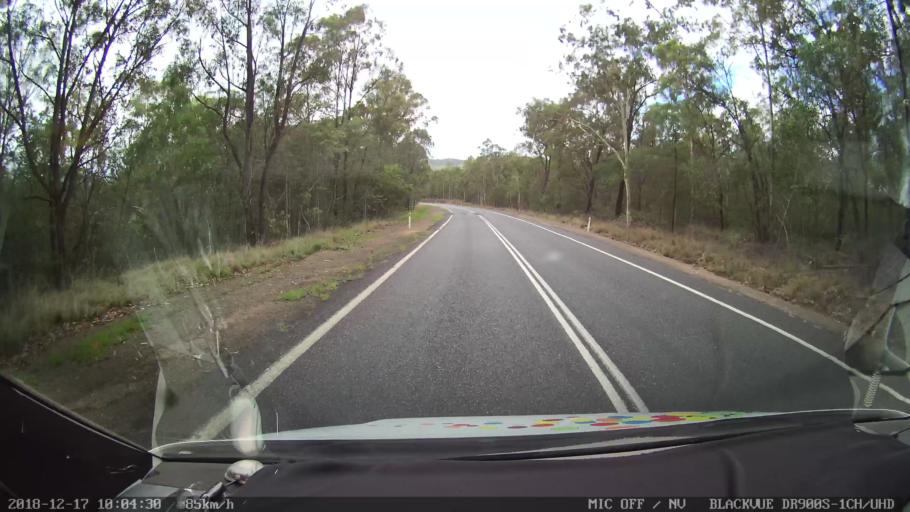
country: AU
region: New South Wales
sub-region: Tenterfield Municipality
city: Carrolls Creek
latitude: -28.8946
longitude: 152.4781
